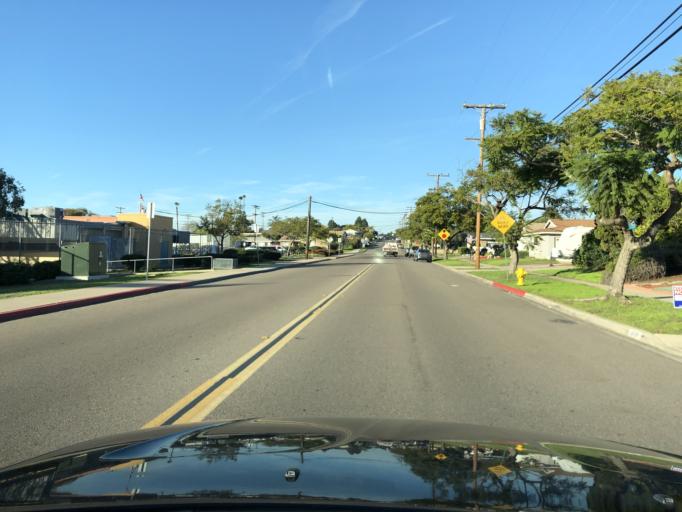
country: US
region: California
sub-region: San Diego County
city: La Jolla
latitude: 32.8198
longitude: -117.1861
